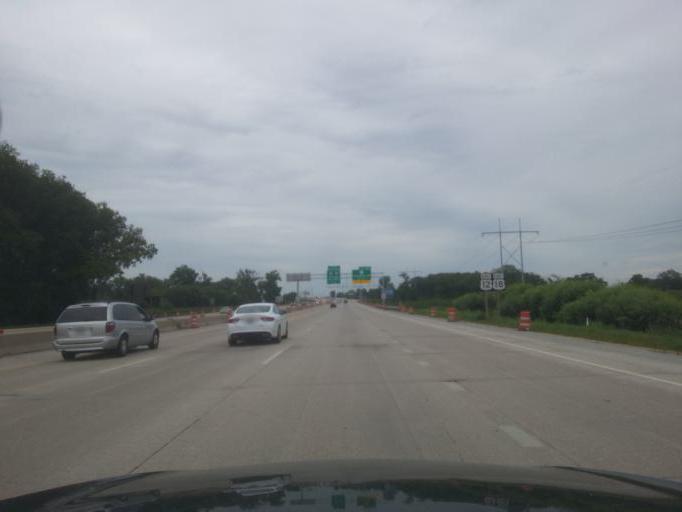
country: US
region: Wisconsin
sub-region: Dane County
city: Monona
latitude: 43.0450
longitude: -89.3186
